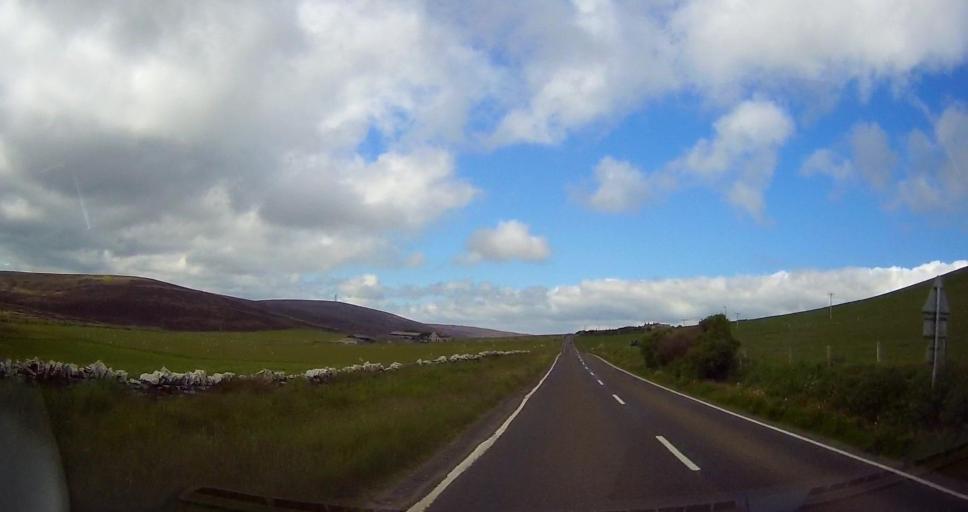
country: GB
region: Scotland
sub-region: Orkney Islands
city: Orkney
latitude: 58.9793
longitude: -3.0249
